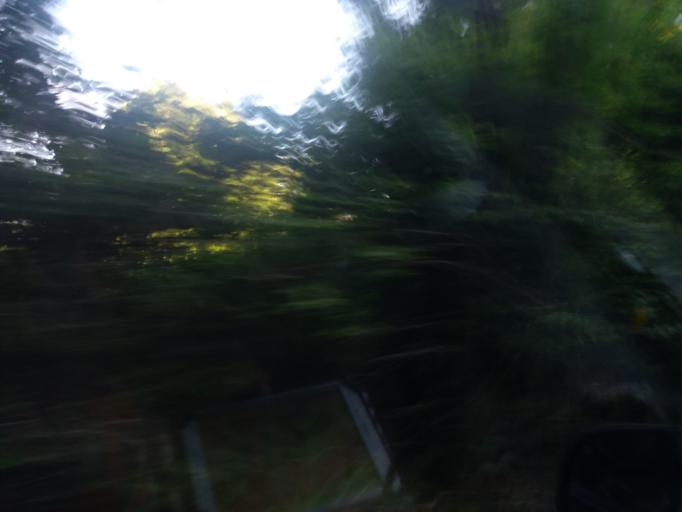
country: IE
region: Leinster
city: Hartstown
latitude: 53.3691
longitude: -6.4099
